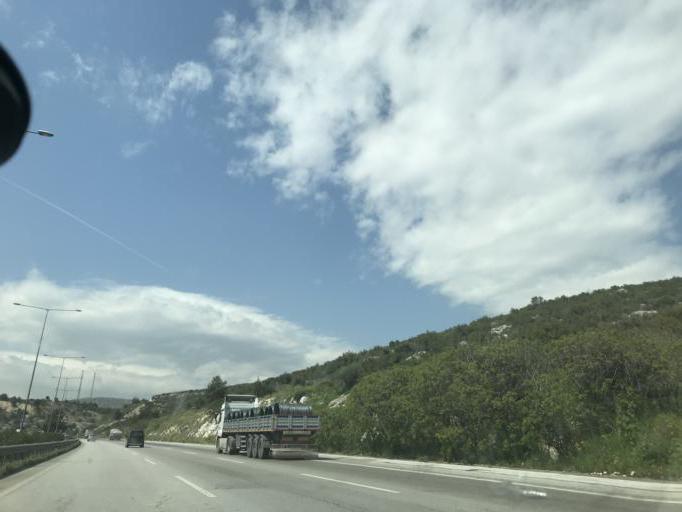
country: TR
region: Mersin
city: Tarsus
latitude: 37.1470
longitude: 34.8416
